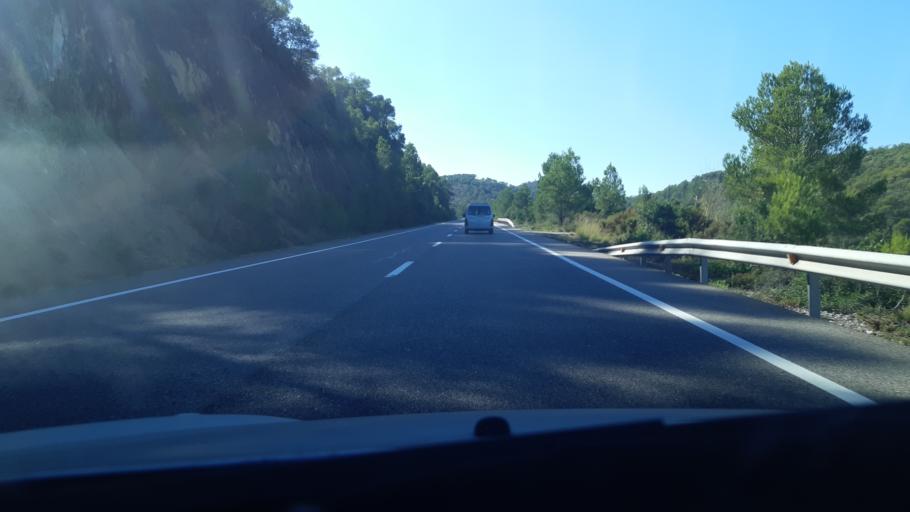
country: ES
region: Catalonia
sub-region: Provincia de Tarragona
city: Rasquera
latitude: 41.0052
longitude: 0.5941
